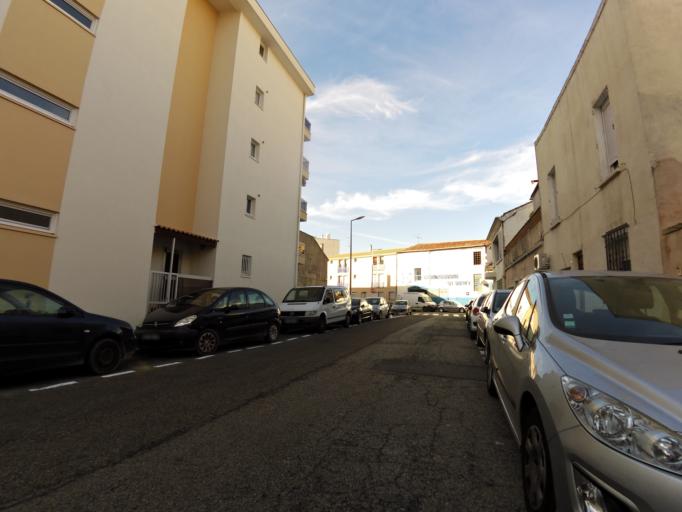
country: FR
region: Languedoc-Roussillon
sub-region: Departement du Gard
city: Nimes
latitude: 43.8297
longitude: 4.3570
